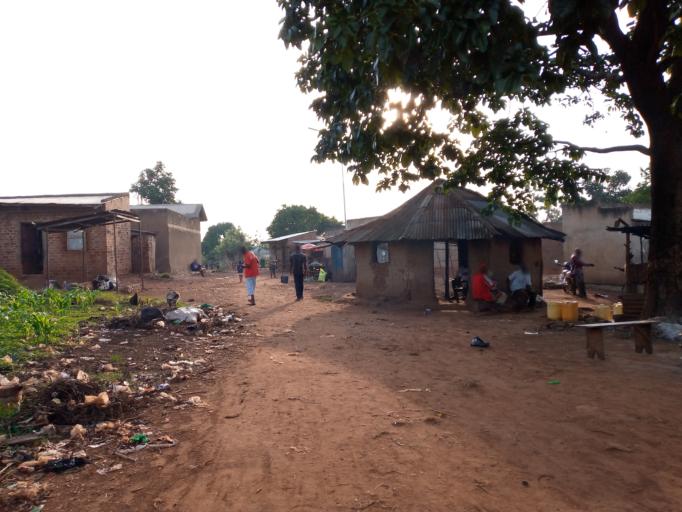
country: UG
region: Eastern Region
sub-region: Mbale District
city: Mbale
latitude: 1.0821
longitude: 34.1557
